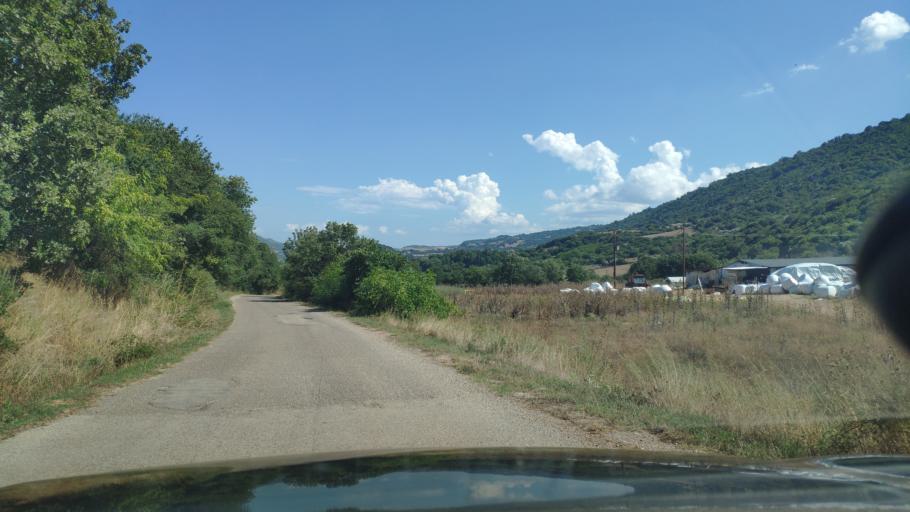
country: GR
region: West Greece
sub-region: Nomos Aitolias kai Akarnanias
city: Katouna
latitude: 38.8441
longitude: 21.0942
